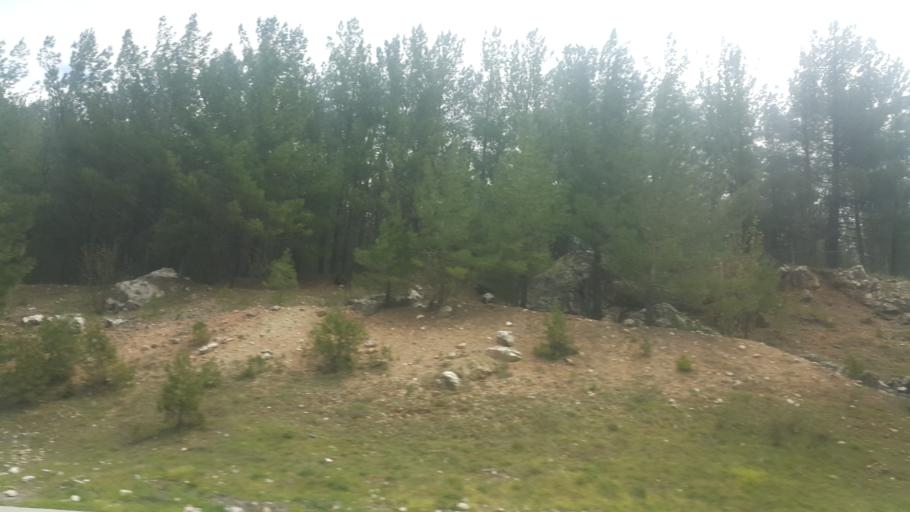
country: TR
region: Adana
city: Pozanti
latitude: 37.3700
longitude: 34.8340
